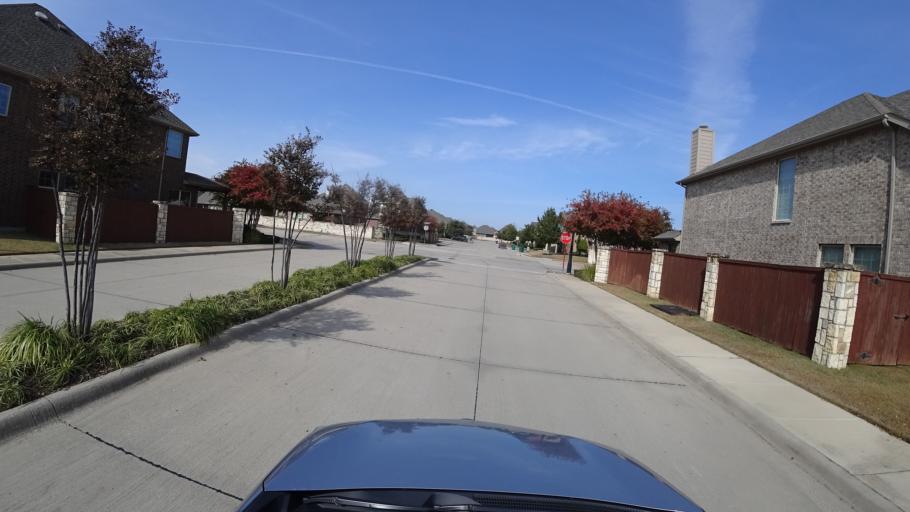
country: US
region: Texas
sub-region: Denton County
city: The Colony
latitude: 33.0559
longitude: -96.9028
